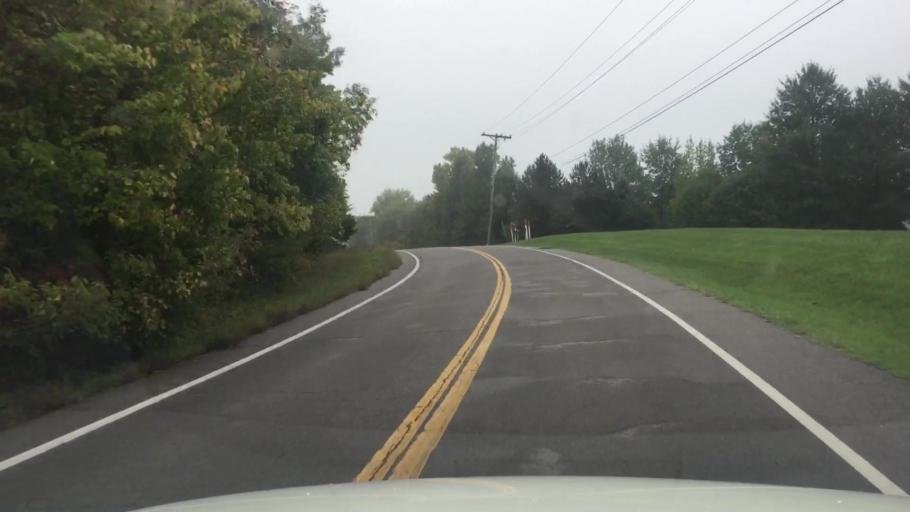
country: US
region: Missouri
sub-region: Boone County
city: Columbia
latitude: 38.8748
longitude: -92.4146
